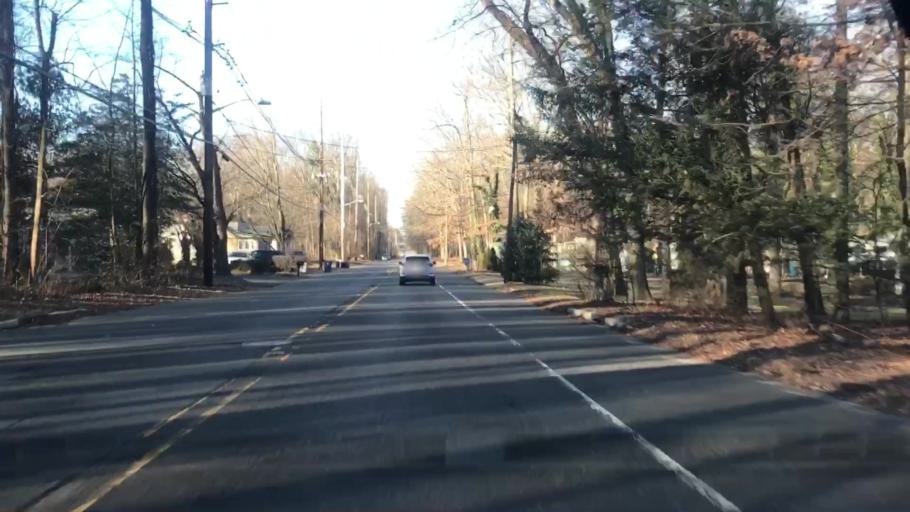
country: US
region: New Jersey
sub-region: Burlington County
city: Burlington
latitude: 40.0503
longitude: -74.8535
